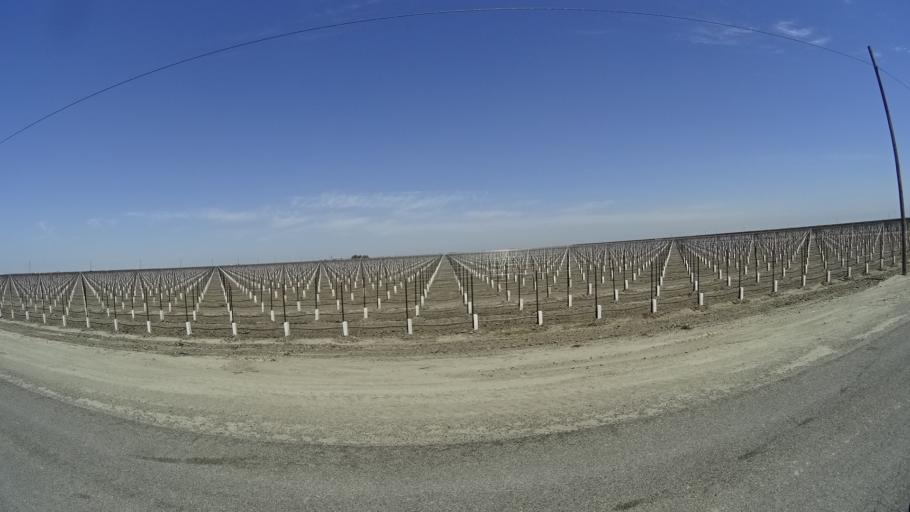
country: US
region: California
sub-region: Kings County
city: Corcoran
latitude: 36.1161
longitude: -119.6402
